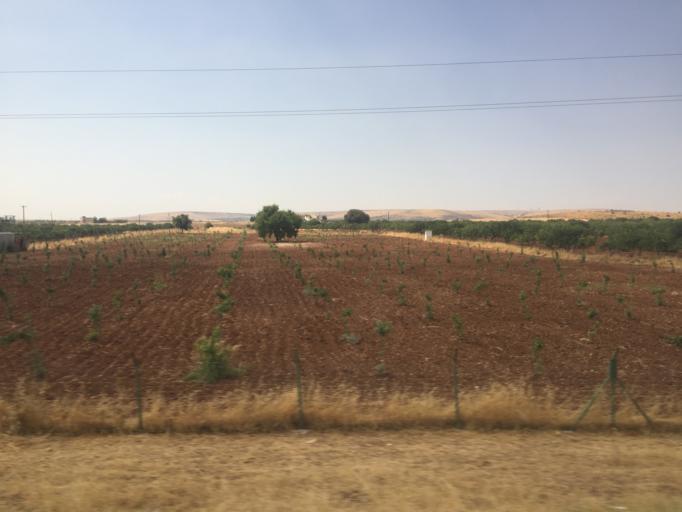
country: TR
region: Sanliurfa
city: Akziyaret
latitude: 37.3890
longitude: 38.8583
